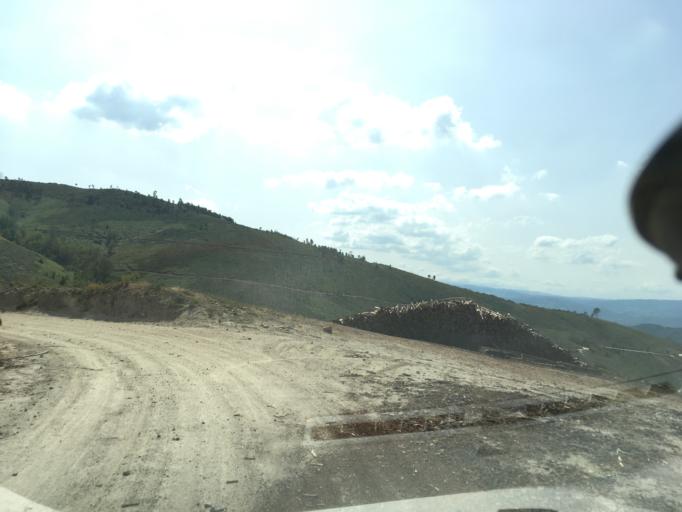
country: PT
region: Braga
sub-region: Celorico de Basto
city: Celorico de Basto
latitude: 41.3000
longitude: -7.9838
